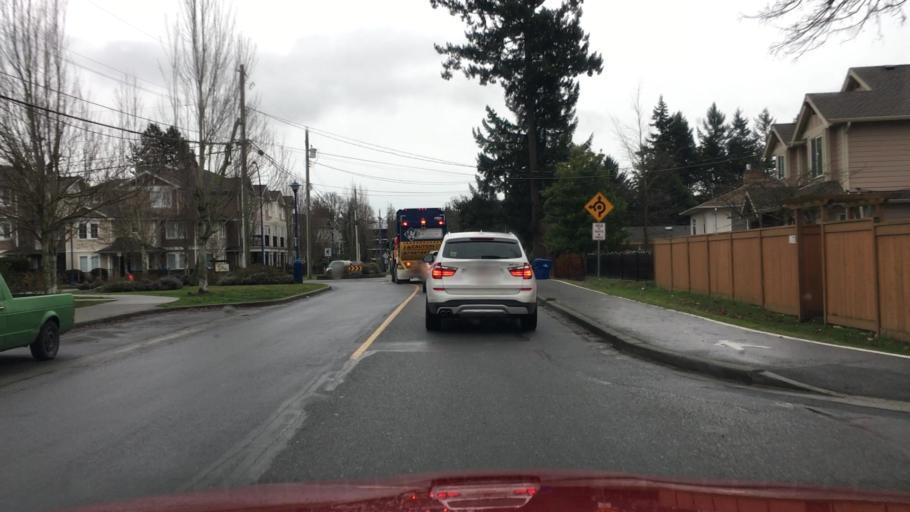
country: CA
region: British Columbia
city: Langford
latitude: 48.4534
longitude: -123.5018
